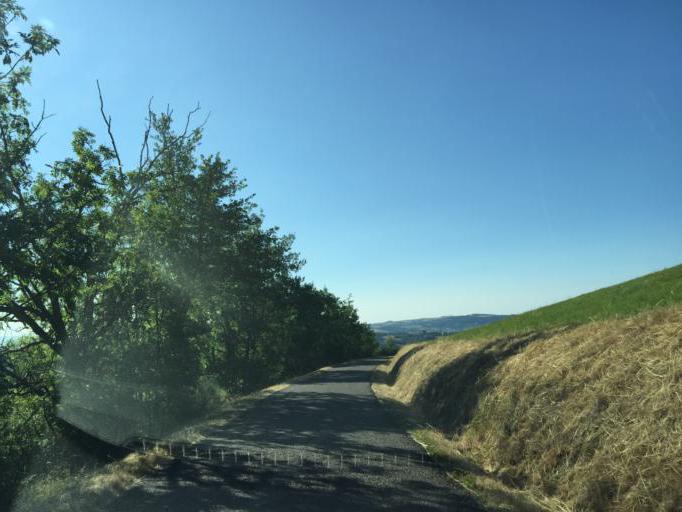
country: FR
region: Rhone-Alpes
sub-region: Departement de la Loire
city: Saint-Jean-Bonnefonds
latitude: 45.4365
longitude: 4.4874
